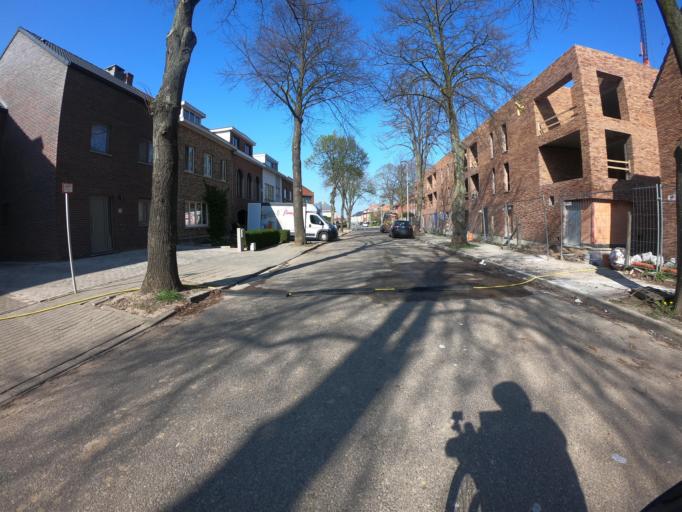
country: BE
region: Flanders
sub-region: Provincie Limburg
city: Sint-Truiden
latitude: 50.8228
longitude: 5.1812
